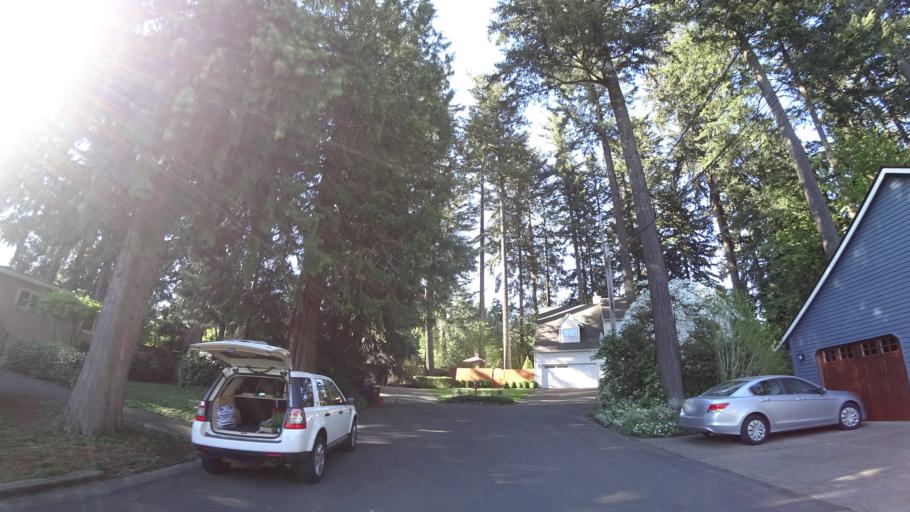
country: US
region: Oregon
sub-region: Washington County
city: West Slope
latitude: 45.5011
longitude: -122.7562
